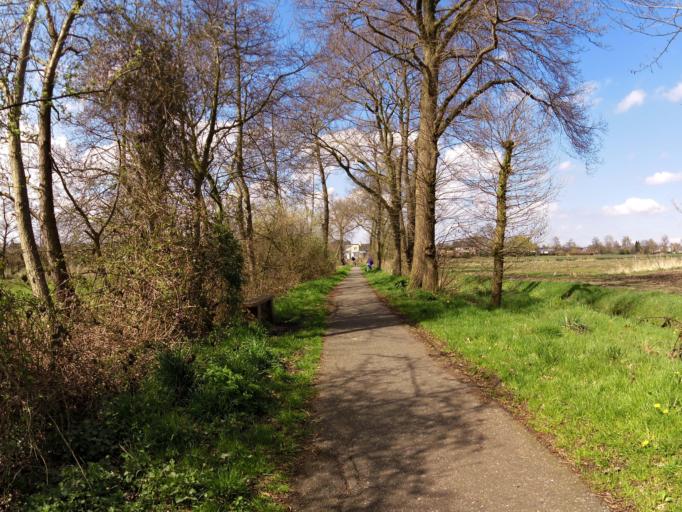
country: NL
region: North Brabant
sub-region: Gemeente Boxtel
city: Boxtel
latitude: 51.6093
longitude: 5.2966
